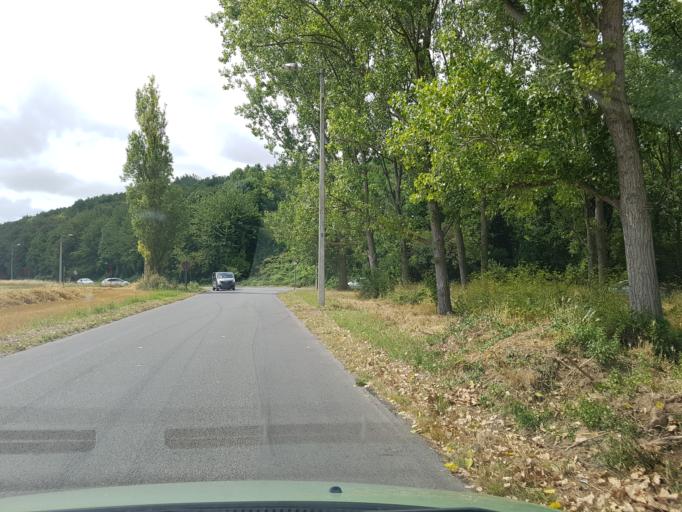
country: FR
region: Nord-Pas-de-Calais
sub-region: Departement du Pas-de-Calais
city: Grenay
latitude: 50.4647
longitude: 2.7449
